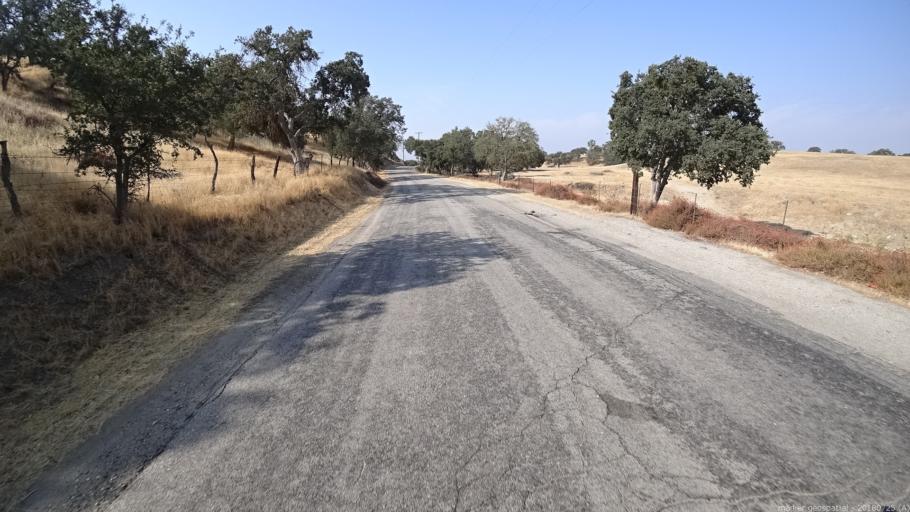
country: US
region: California
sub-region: San Luis Obispo County
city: San Miguel
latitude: 35.7556
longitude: -120.6079
